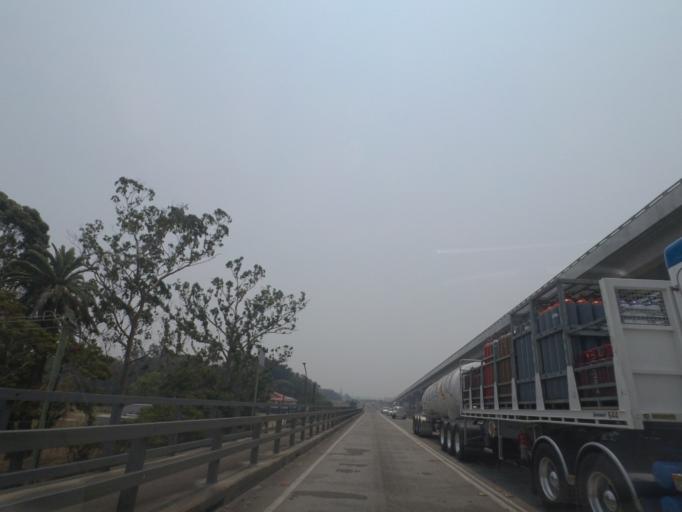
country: AU
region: New South Wales
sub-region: Clarence Valley
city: Maclean
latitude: -29.4274
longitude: 153.2410
